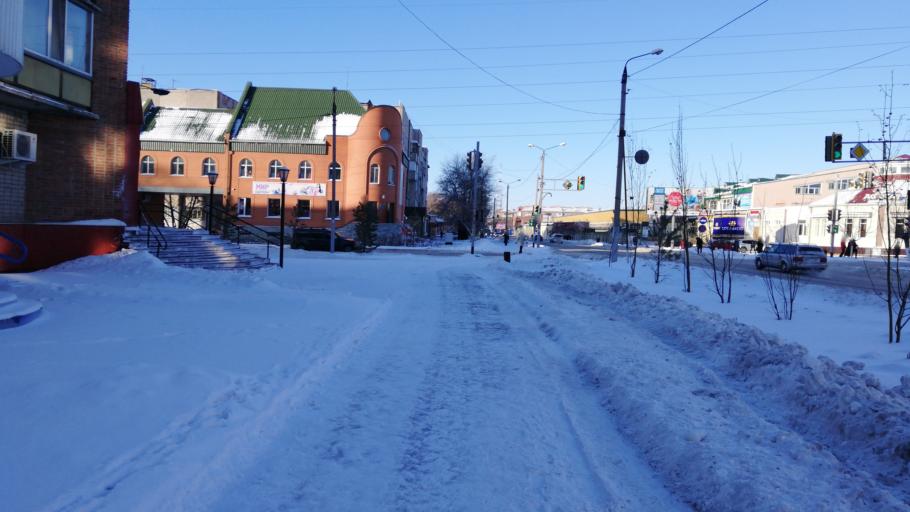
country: KZ
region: Soltustik Qazaqstan
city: Petropavlovsk
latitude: 54.8618
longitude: 69.1483
